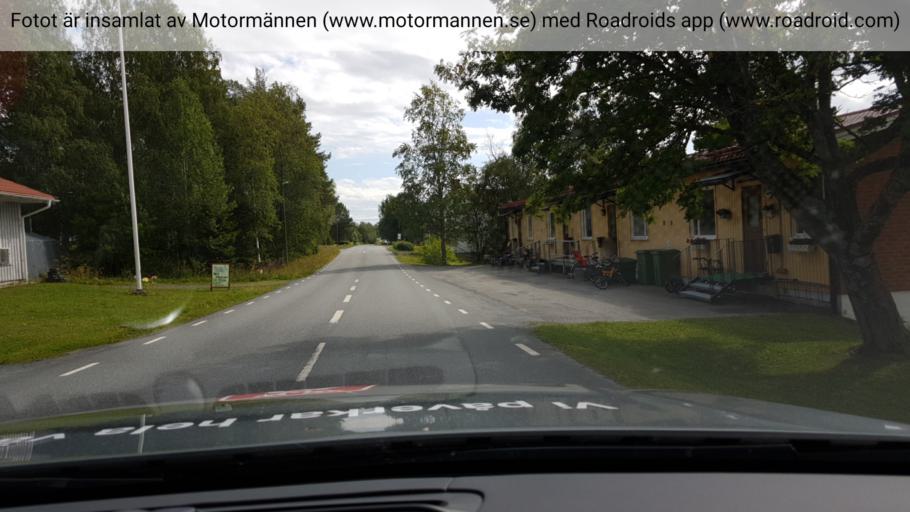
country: SE
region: Jaemtland
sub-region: Krokoms Kommun
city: Valla
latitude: 63.3328
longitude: 14.0147
